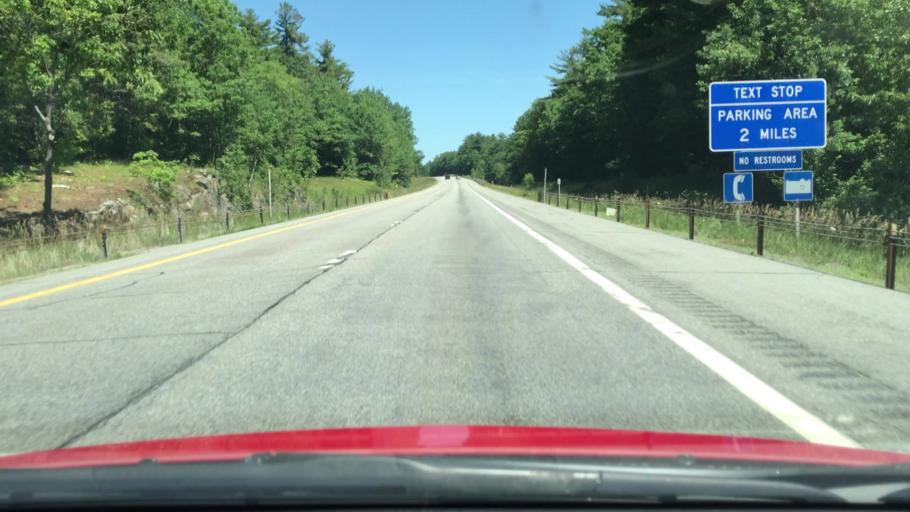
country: US
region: New York
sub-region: Essex County
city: Mineville
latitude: 44.1309
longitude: -73.5888
